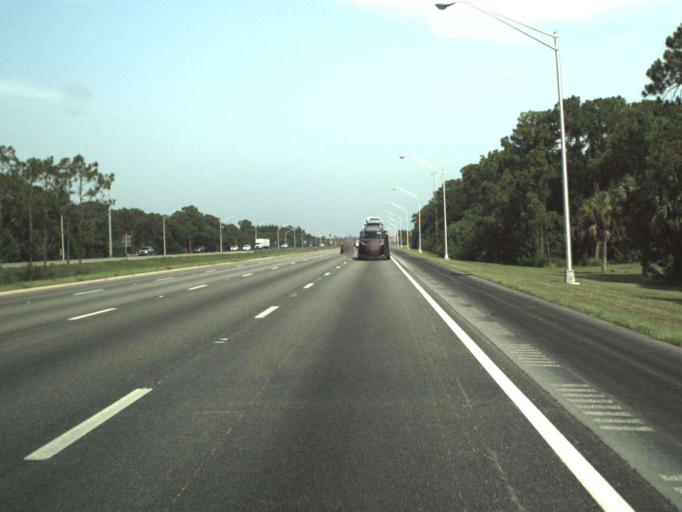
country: US
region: Florida
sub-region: Saint Lucie County
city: Lakewood Park
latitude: 27.4661
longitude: -80.4210
